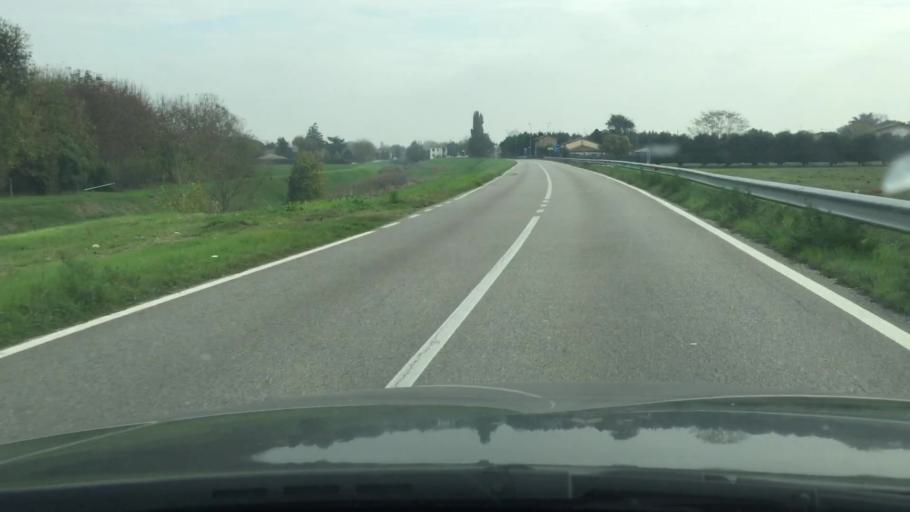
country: IT
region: Emilia-Romagna
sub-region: Provincia di Ferrara
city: Porotto-Cassama
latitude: 44.8421
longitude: 11.5731
